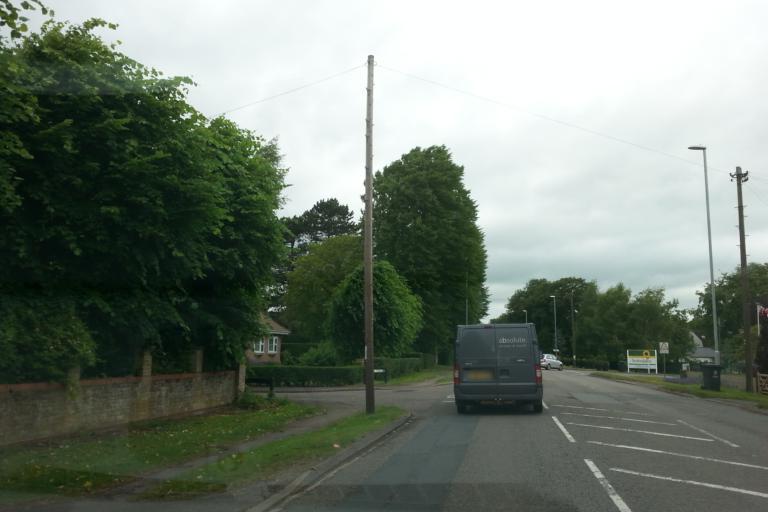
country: GB
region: England
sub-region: Cambridgeshire
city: Cambridge
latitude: 52.1595
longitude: 0.1265
